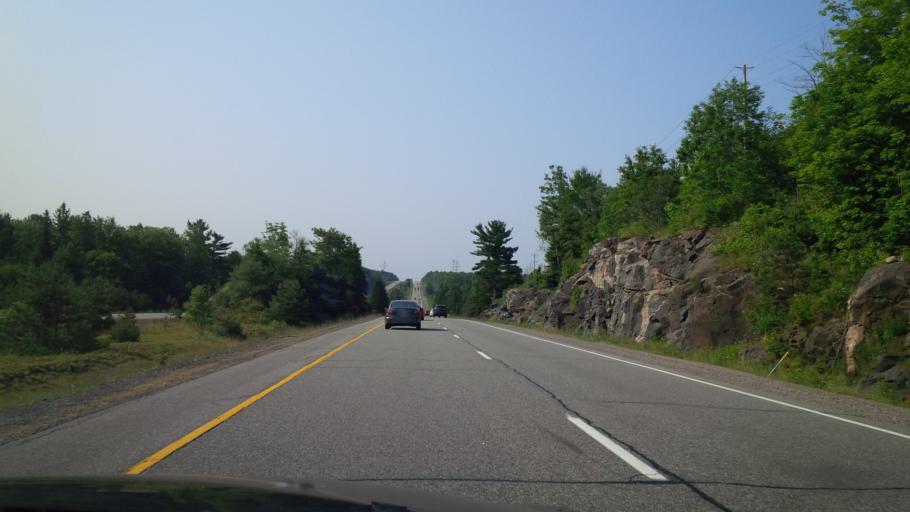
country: CA
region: Ontario
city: Bracebridge
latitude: 45.1720
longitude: -79.3120
